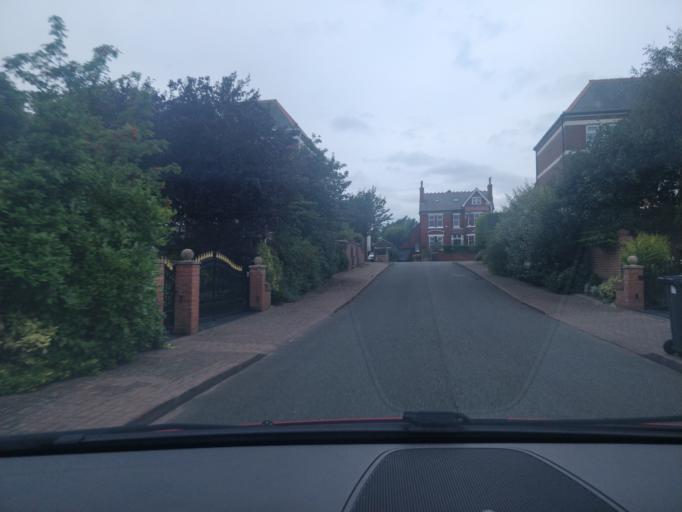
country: GB
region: England
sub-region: Sefton
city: Southport
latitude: 53.6343
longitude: -3.0302
